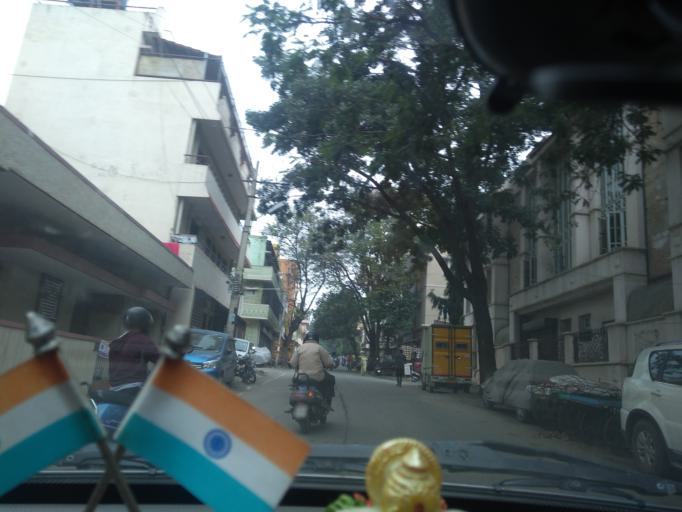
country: IN
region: Karnataka
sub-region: Bangalore Urban
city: Bangalore
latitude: 12.9827
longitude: 77.5556
